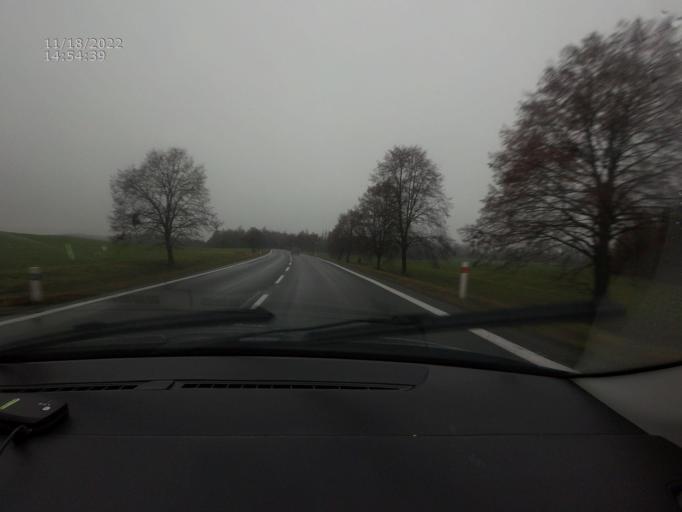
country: CZ
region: Jihocesky
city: Milevsko
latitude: 49.4634
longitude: 14.3260
